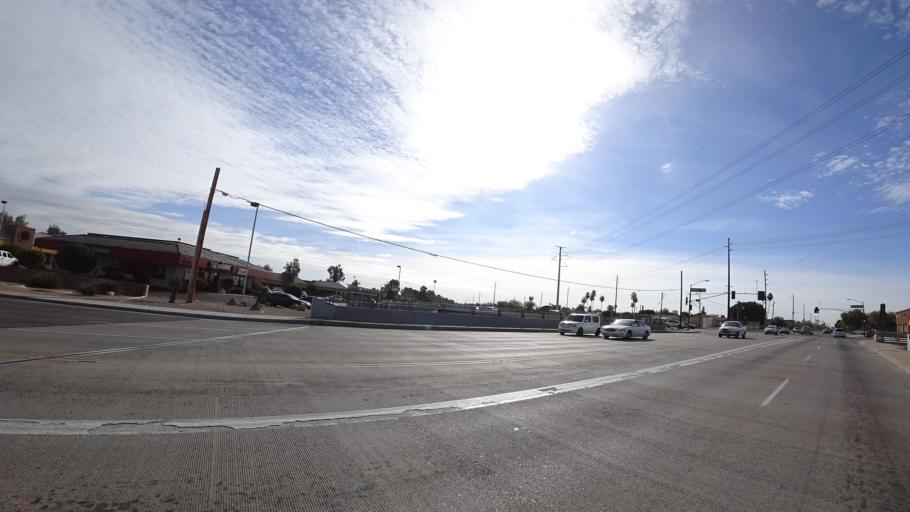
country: US
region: Arizona
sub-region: Maricopa County
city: Glendale
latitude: 33.5827
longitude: -112.1516
